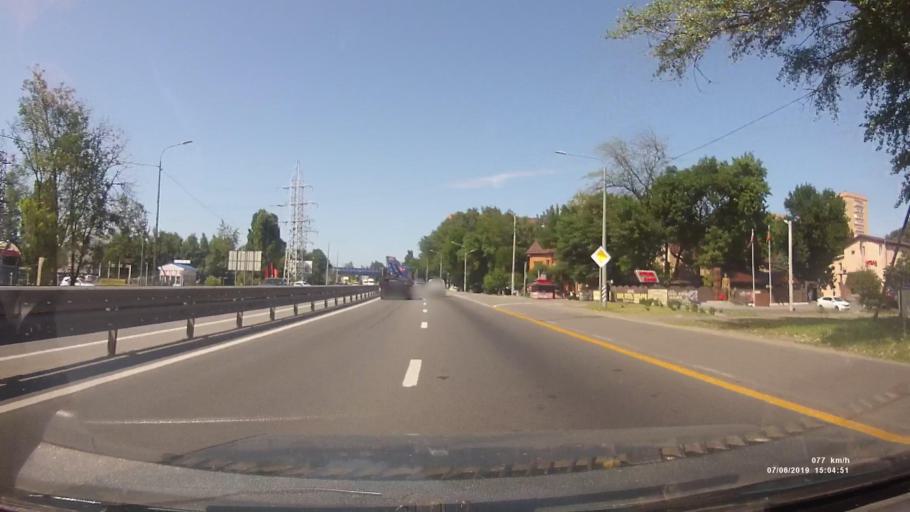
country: RU
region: Rostov
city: Aksay
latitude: 47.2664
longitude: 39.8545
